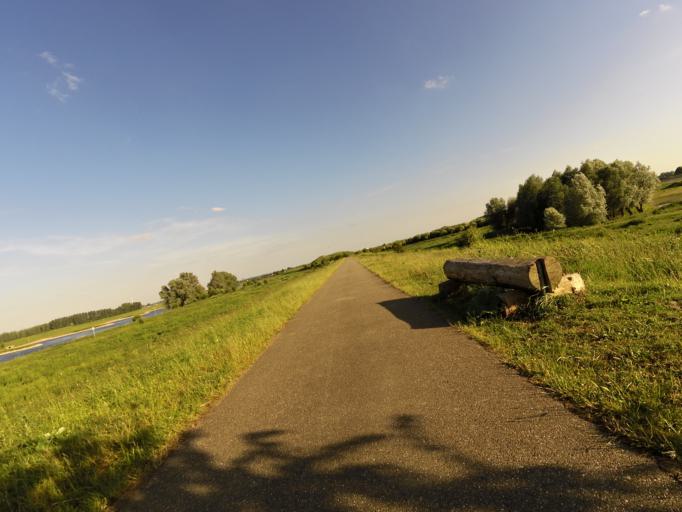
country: NL
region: Gelderland
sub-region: Gemeente Duiven
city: Duiven
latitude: 51.8855
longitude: 6.0244
